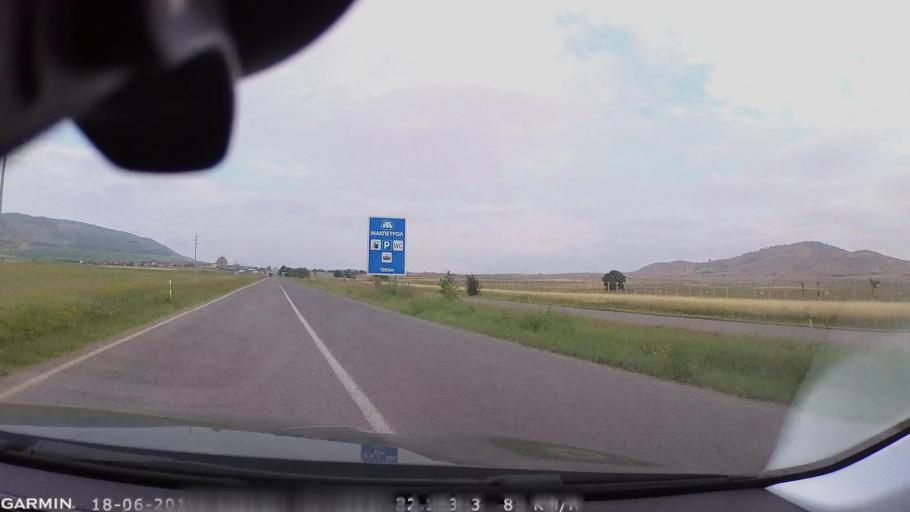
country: MK
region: Stip
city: Shtip
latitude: 41.7672
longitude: 22.1536
